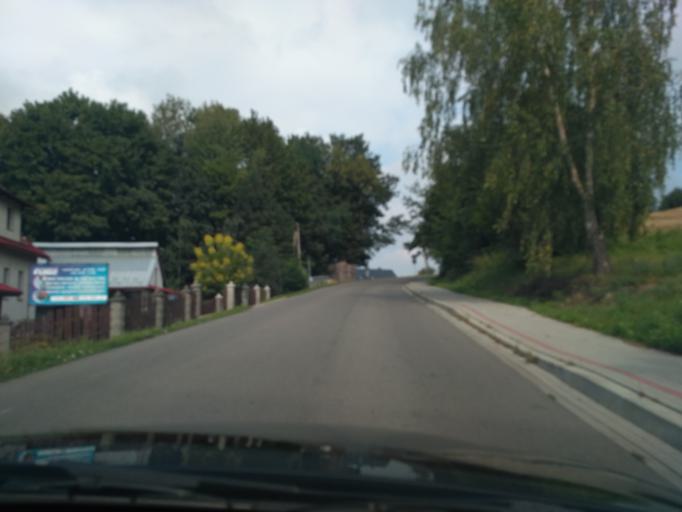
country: PL
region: Subcarpathian Voivodeship
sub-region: Powiat strzyzowski
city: Czudec
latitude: 49.9503
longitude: 21.8459
